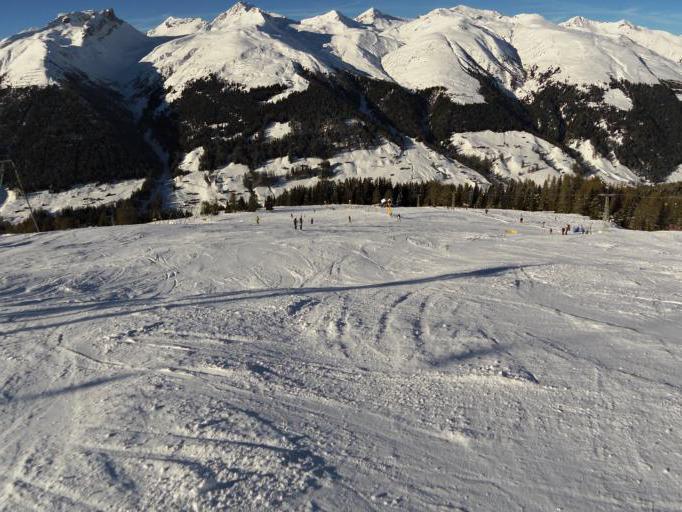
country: CH
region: Grisons
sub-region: Praettigau/Davos District
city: Davos
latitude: 46.7452
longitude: 9.8055
